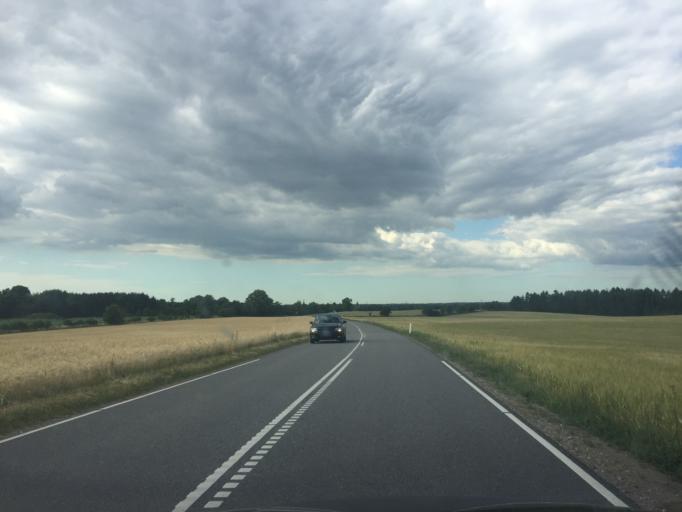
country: DK
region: Capital Region
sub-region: Egedal Kommune
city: Vekso
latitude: 55.7183
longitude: 12.2085
